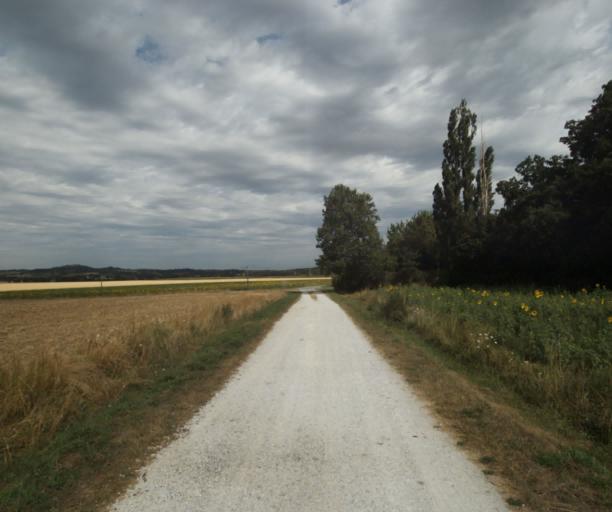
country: FR
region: Midi-Pyrenees
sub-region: Departement de la Haute-Garonne
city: Saint-Felix-Lauragais
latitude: 43.4413
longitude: 1.9377
